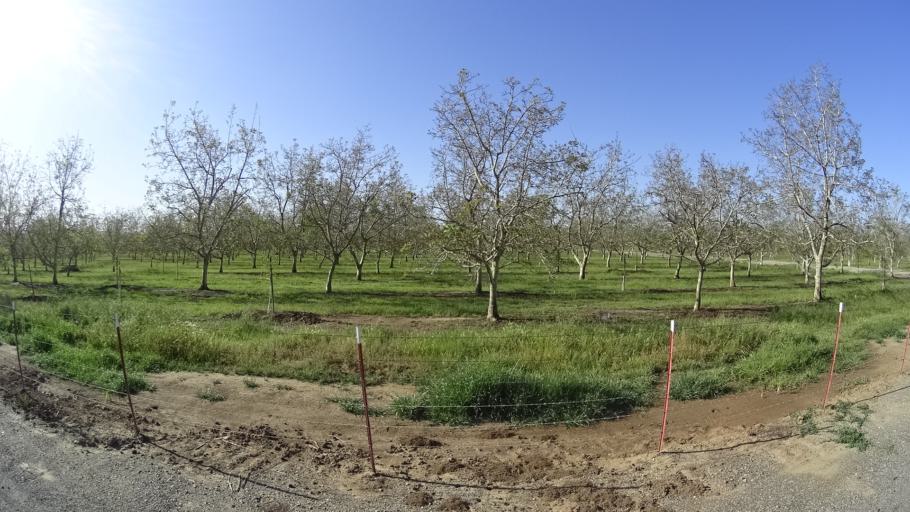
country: US
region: California
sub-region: Glenn County
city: Hamilton City
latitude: 39.6960
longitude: -122.0786
